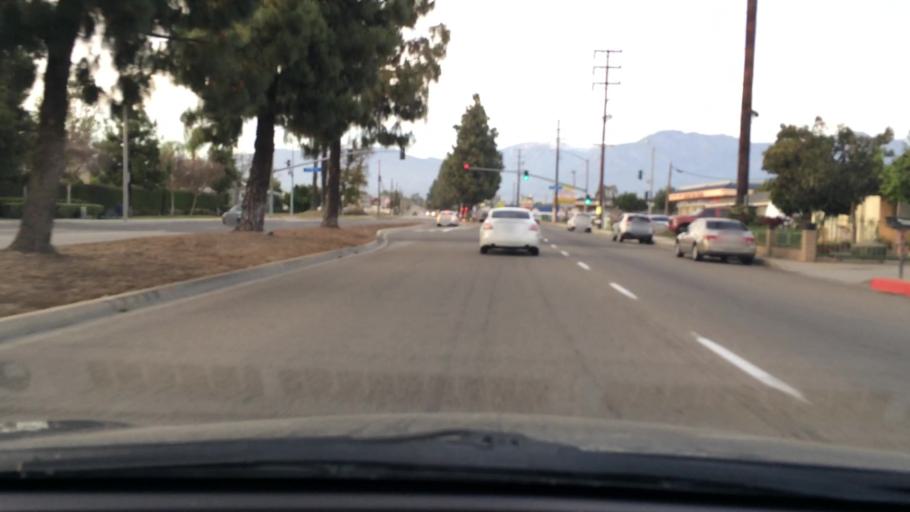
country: US
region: California
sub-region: San Bernardino County
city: Montclair
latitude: 34.0513
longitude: -117.6895
